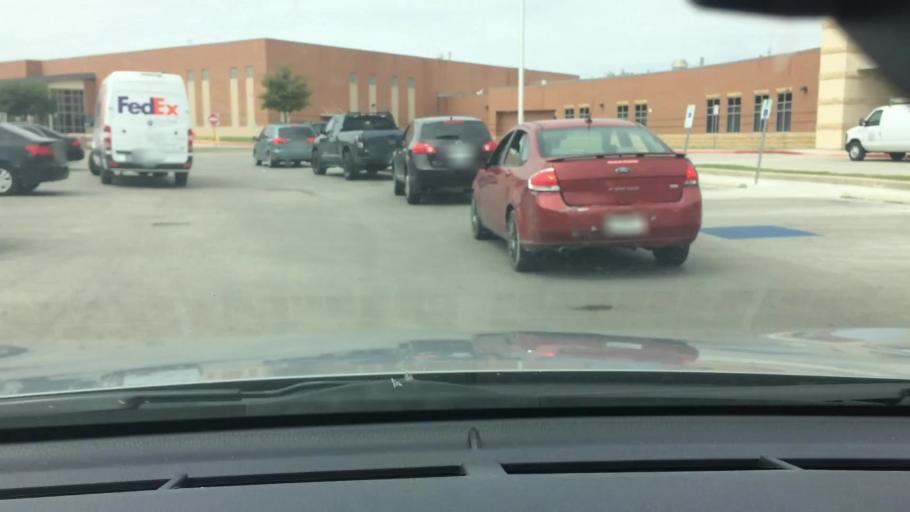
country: US
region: Texas
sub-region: Bexar County
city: Converse
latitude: 29.5090
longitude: -98.3029
